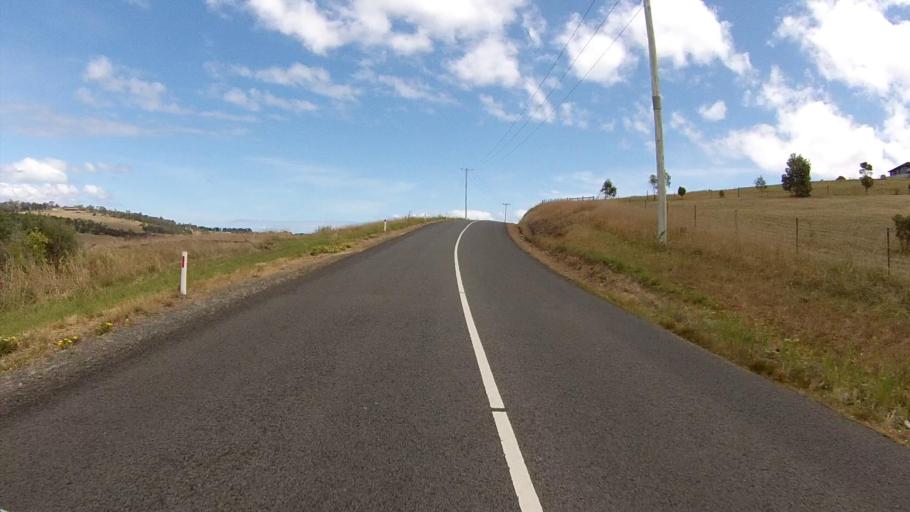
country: AU
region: Tasmania
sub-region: Sorell
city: Sorell
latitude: -42.8682
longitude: 147.6734
